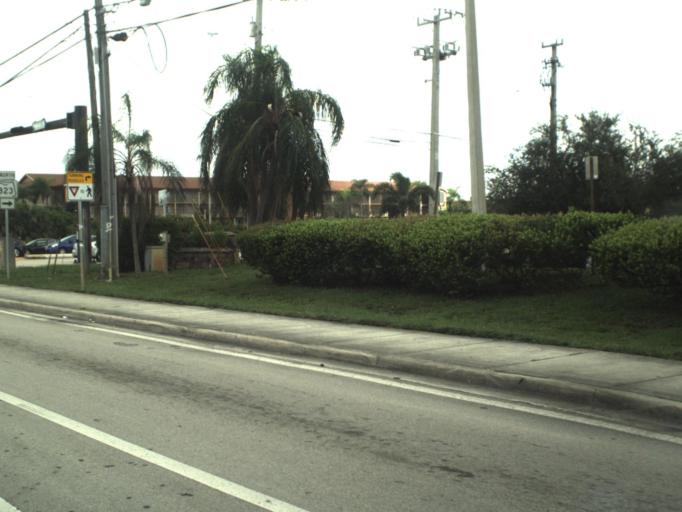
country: US
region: Florida
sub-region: Miami-Dade County
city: Country Club
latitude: 25.9933
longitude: -80.3109
